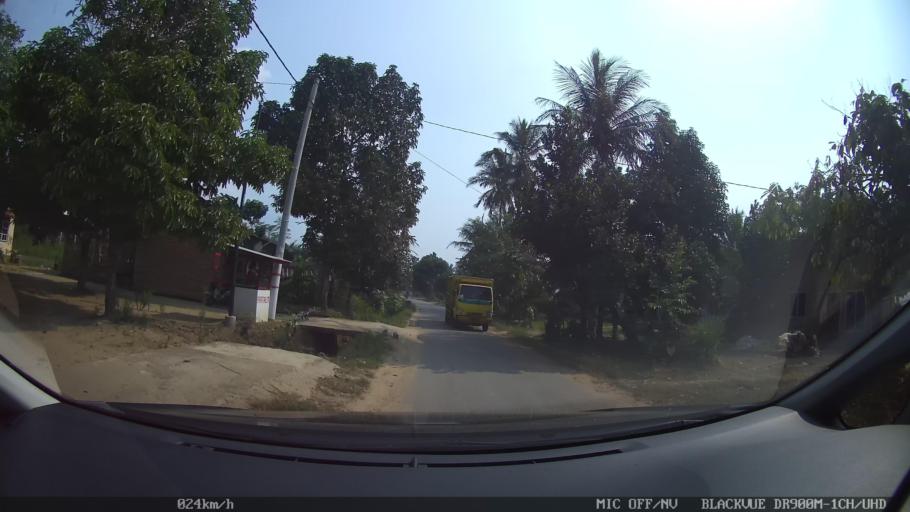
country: ID
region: Lampung
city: Pringsewu
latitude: -5.3929
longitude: 104.9930
